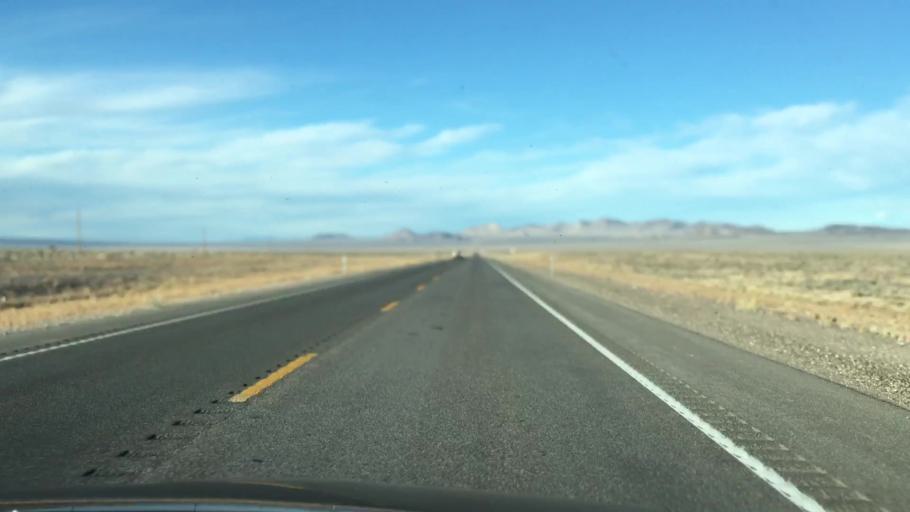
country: US
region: Nevada
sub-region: Esmeralda County
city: Goldfield
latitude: 37.8039
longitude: -117.2395
